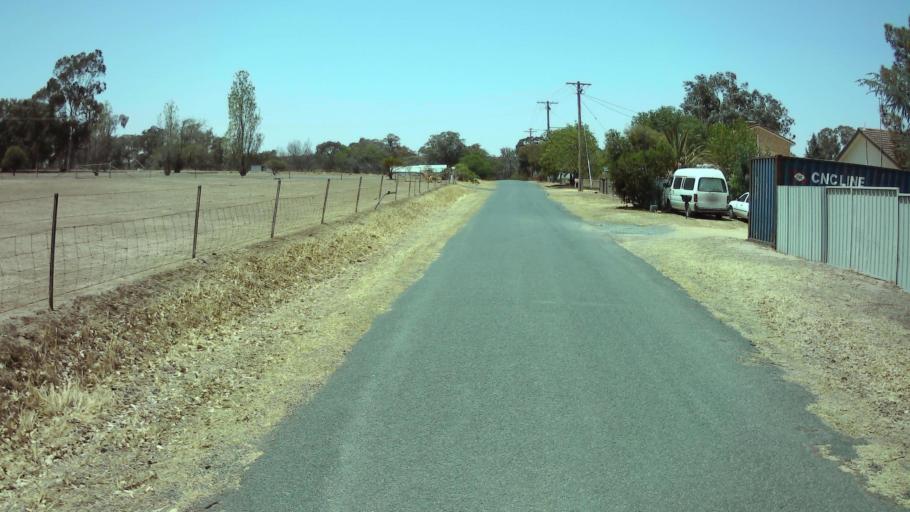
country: AU
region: New South Wales
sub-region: Weddin
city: Grenfell
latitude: -33.8878
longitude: 148.1650
